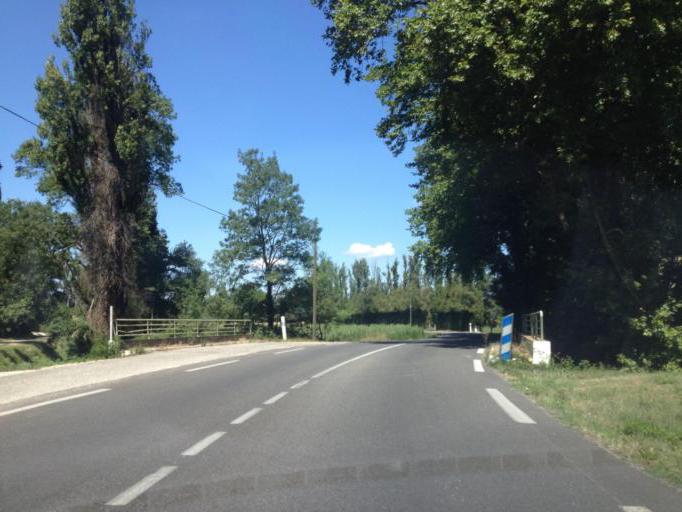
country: FR
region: Languedoc-Roussillon
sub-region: Departement du Gard
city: Sauveterre
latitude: 44.0053
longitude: 4.8107
